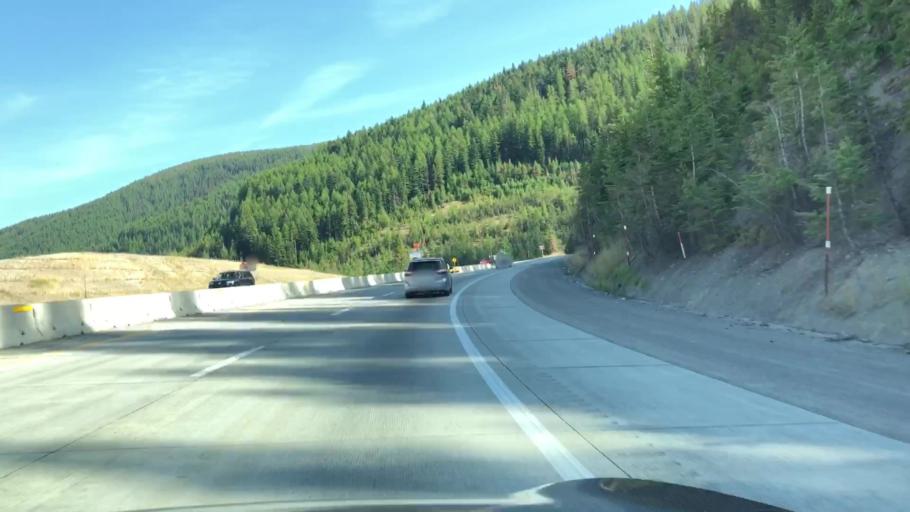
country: US
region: Idaho
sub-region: Shoshone County
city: Wallace
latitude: 47.4625
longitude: -115.7385
